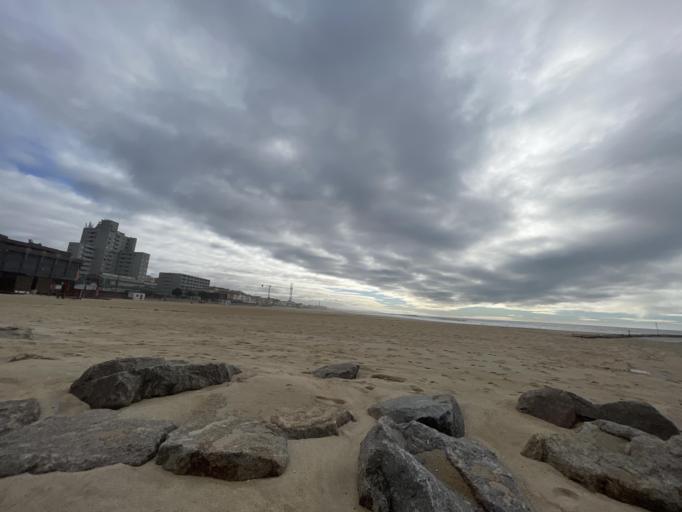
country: PT
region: Aveiro
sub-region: Espinho
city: Espinho
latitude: 41.0099
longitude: -8.6470
